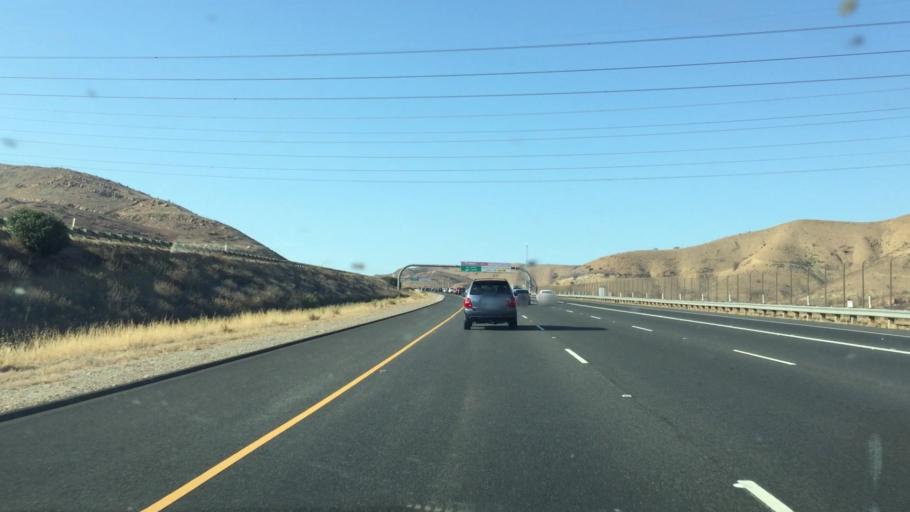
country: US
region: California
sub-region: Orange County
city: North Tustin
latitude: 33.8141
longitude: -117.7194
